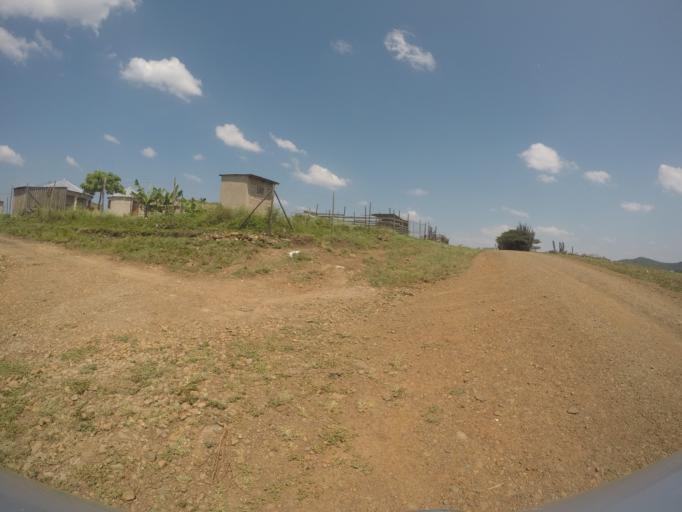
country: ZA
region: KwaZulu-Natal
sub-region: uThungulu District Municipality
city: Empangeni
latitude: -28.5905
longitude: 31.7365
